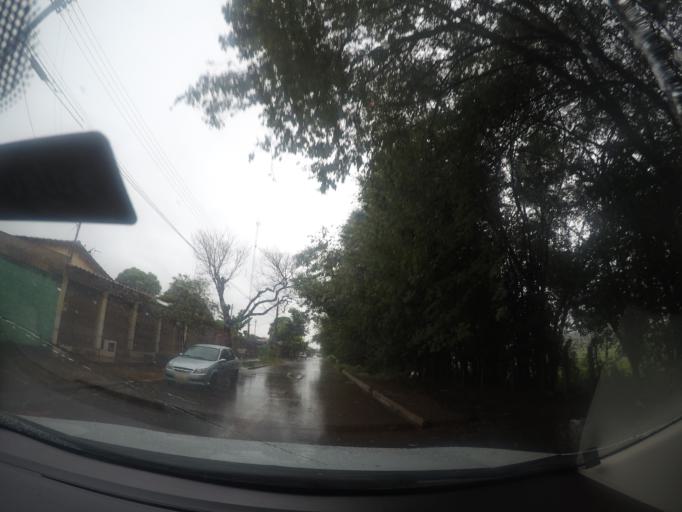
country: BR
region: Goias
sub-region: Goianira
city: Goianira
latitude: -16.5947
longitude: -49.3540
